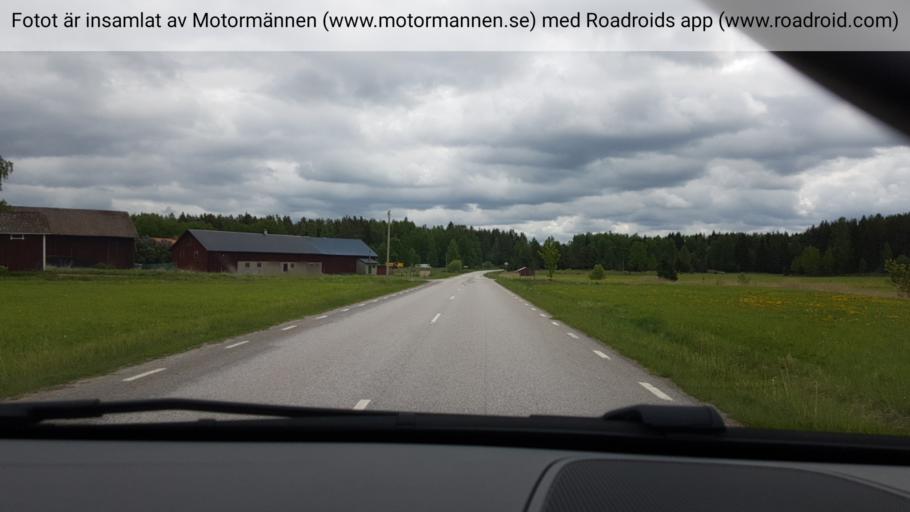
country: SE
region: Uppsala
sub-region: Heby Kommun
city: Tarnsjo
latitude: 60.1136
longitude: 17.0331
